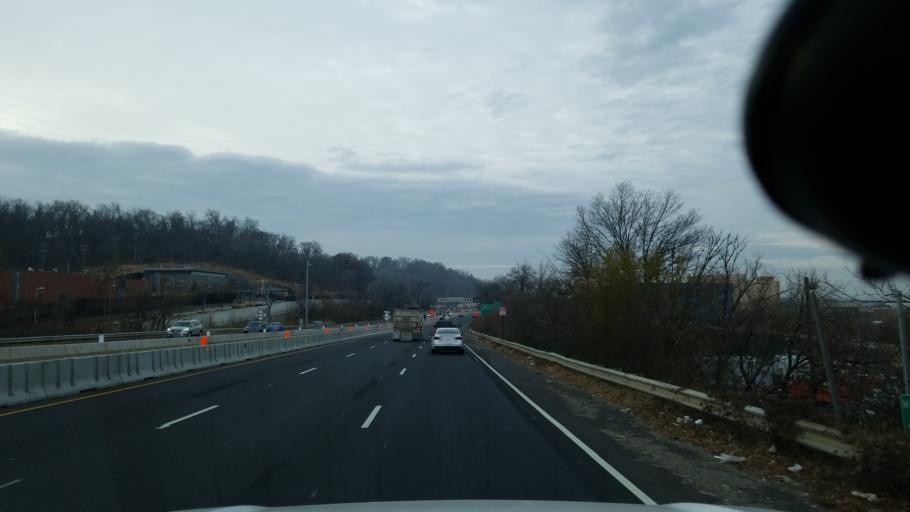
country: US
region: Maryland
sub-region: Prince George's County
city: Glassmanor
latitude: 38.8593
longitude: -77.0035
